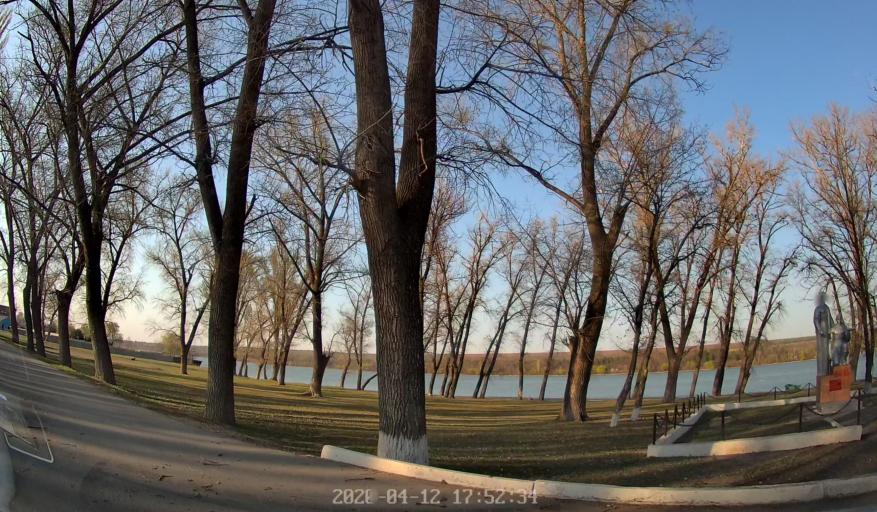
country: MD
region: Telenesti
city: Cocieri
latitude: 47.3827
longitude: 29.1247
